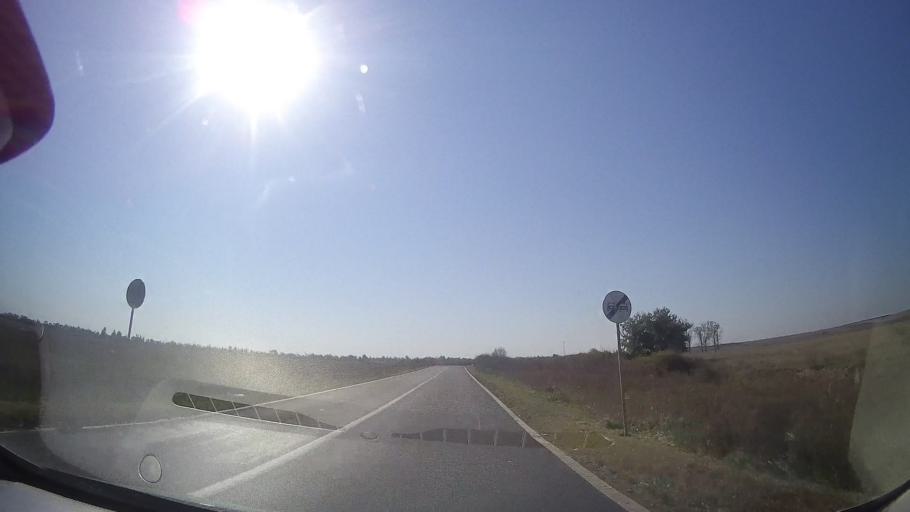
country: RO
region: Timis
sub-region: Comuna Belint
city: Belint
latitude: 45.7775
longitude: 21.7315
